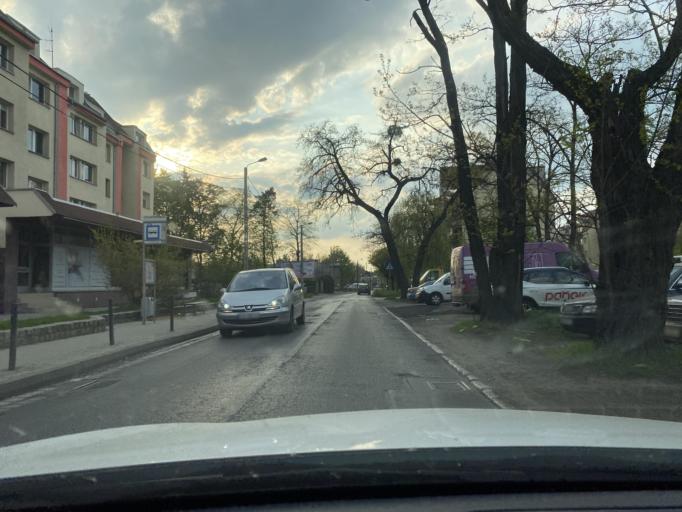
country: PL
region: Lower Silesian Voivodeship
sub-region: Powiat wroclawski
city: Wroclaw
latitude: 51.1392
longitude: 17.0654
